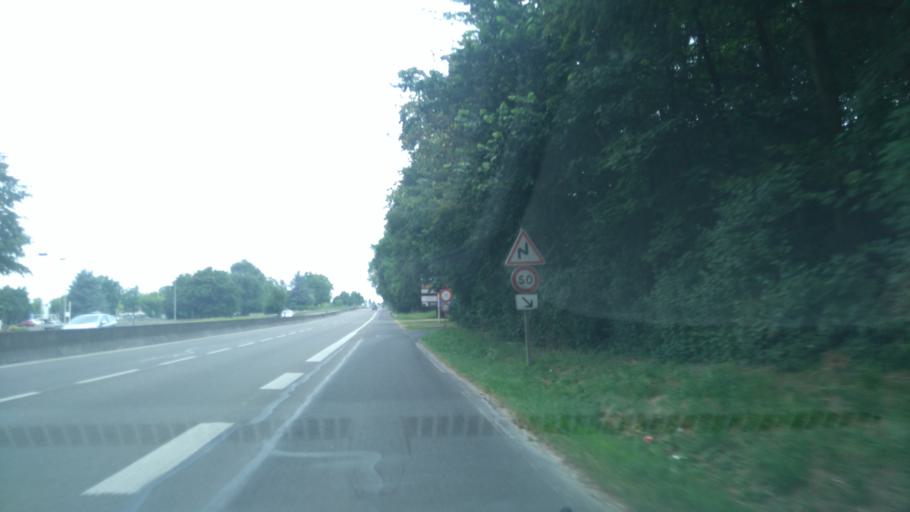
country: FR
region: Picardie
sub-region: Departement de l'Oise
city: Saint-Maximin
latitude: 49.2318
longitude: 2.4708
